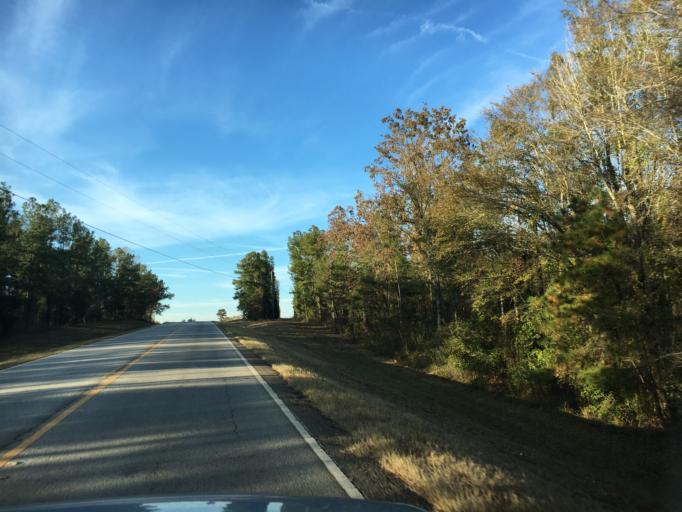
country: US
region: Georgia
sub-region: Elbert County
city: Elberton
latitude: 33.9959
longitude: -82.7794
